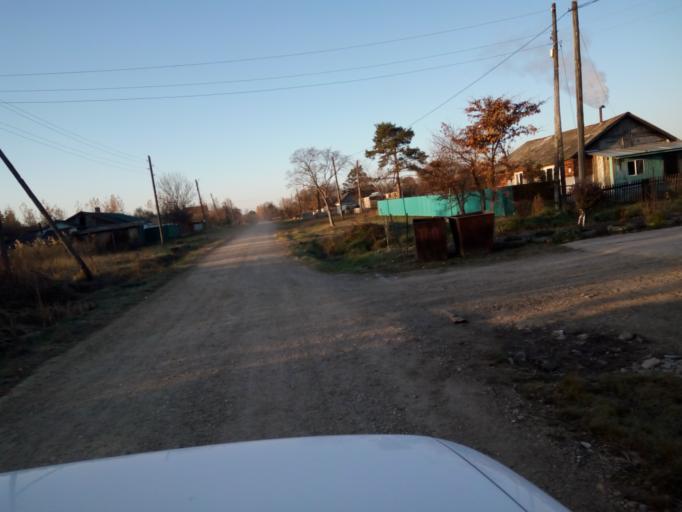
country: RU
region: Primorskiy
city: Lazo
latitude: 45.8803
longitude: 133.6533
